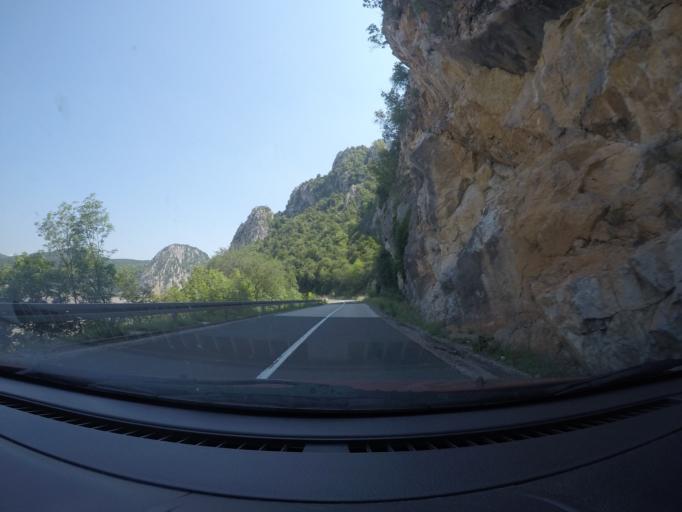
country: RO
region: Mehedinti
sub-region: Comuna Dubova
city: Dubova
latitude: 44.6211
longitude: 22.2767
